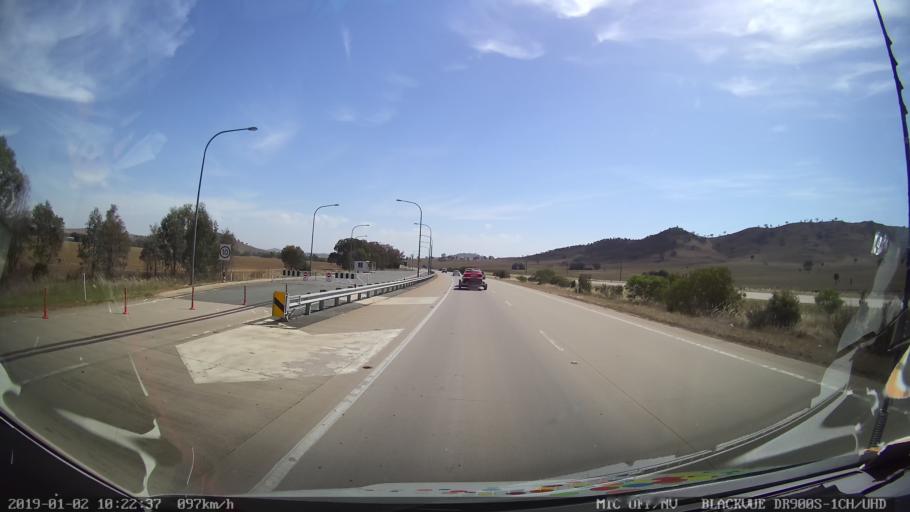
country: AU
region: New South Wales
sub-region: Gundagai
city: Gundagai
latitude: -34.9700
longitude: 148.1502
